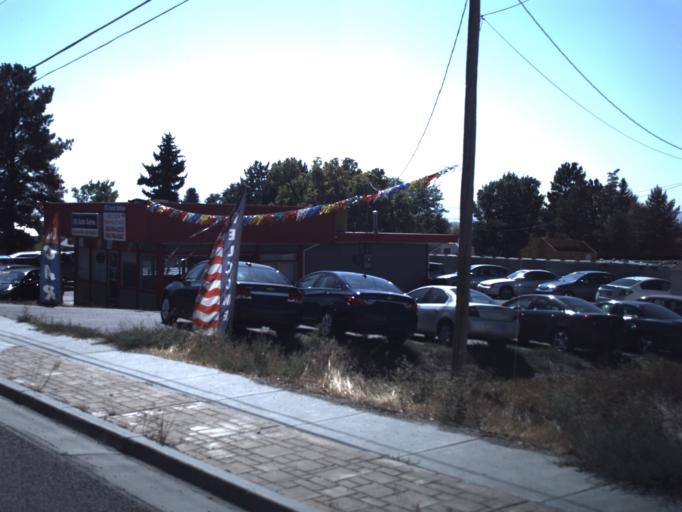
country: US
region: Utah
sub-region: Cache County
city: Richmond
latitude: 41.9211
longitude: -111.8145
